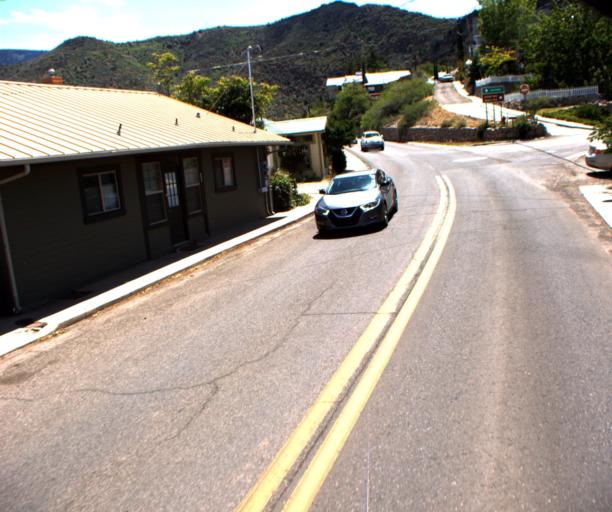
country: US
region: Arizona
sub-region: Yavapai County
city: Clarkdale
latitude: 34.7494
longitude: -112.1087
